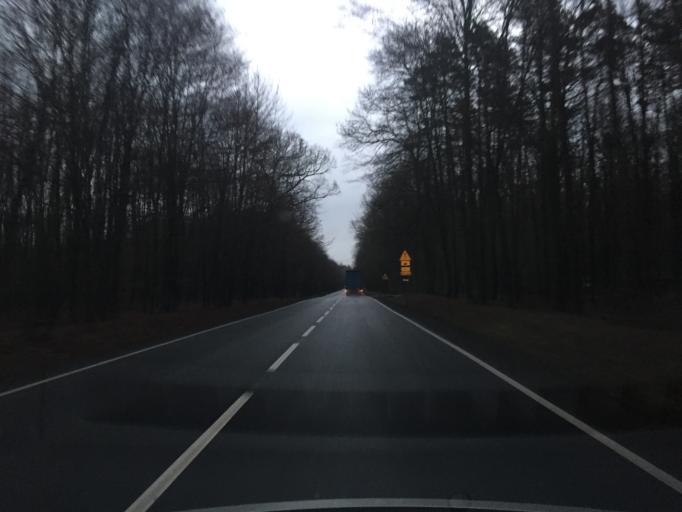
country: PL
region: Kujawsko-Pomorskie
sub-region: Powiat brodnicki
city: Bobrowo
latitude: 53.2555
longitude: 19.3219
